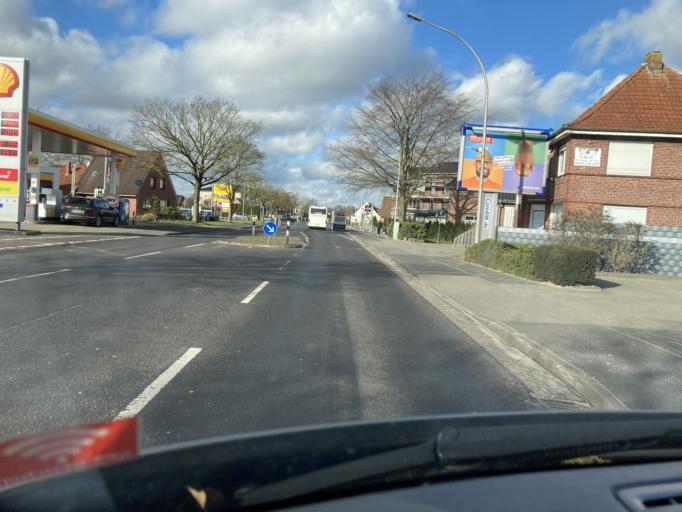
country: DE
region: Lower Saxony
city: Ostrhauderfehn
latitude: 53.1382
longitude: 7.5710
